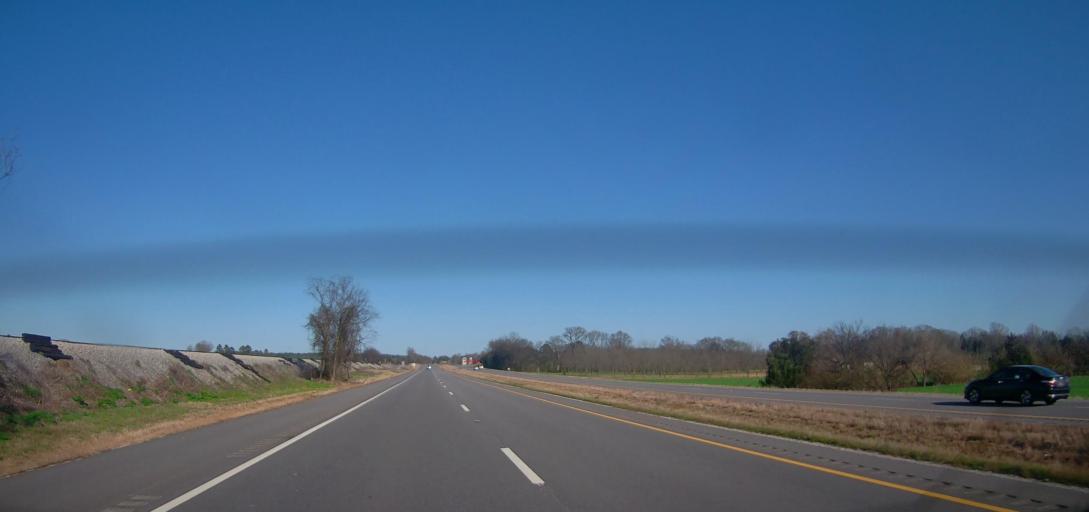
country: US
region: Alabama
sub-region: Colbert County
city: Cherokee
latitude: 34.7598
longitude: -88.0010
